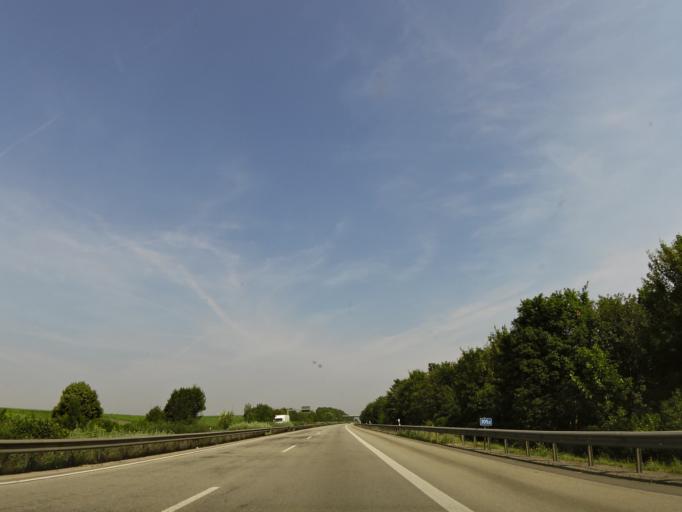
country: DE
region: Rheinland-Pfalz
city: Sprendlingen
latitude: 49.8479
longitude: 7.9826
